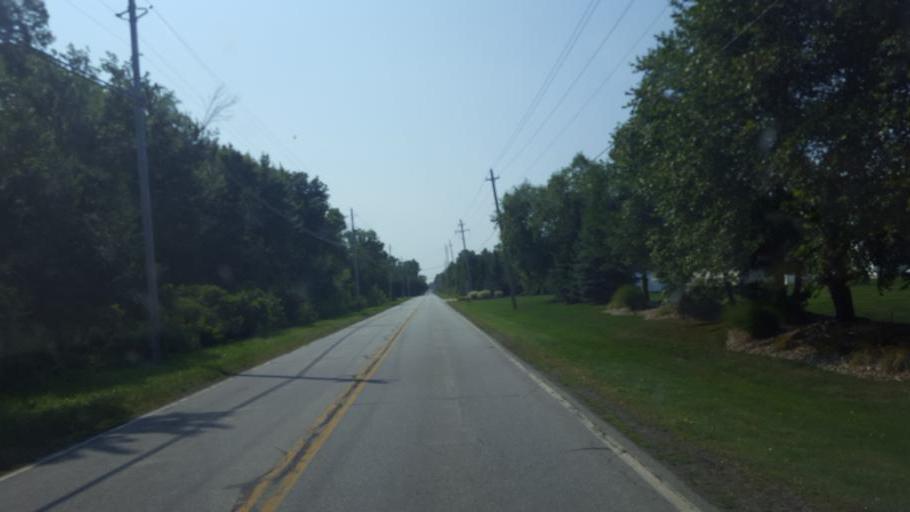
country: US
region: Ohio
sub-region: Lake County
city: Painesville
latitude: 41.7685
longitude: -81.2080
